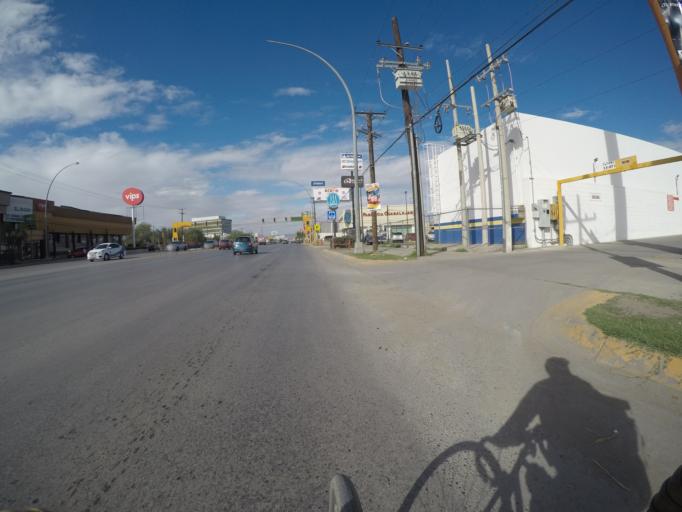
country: MX
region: Chihuahua
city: Ciudad Juarez
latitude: 31.7392
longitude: -106.4295
